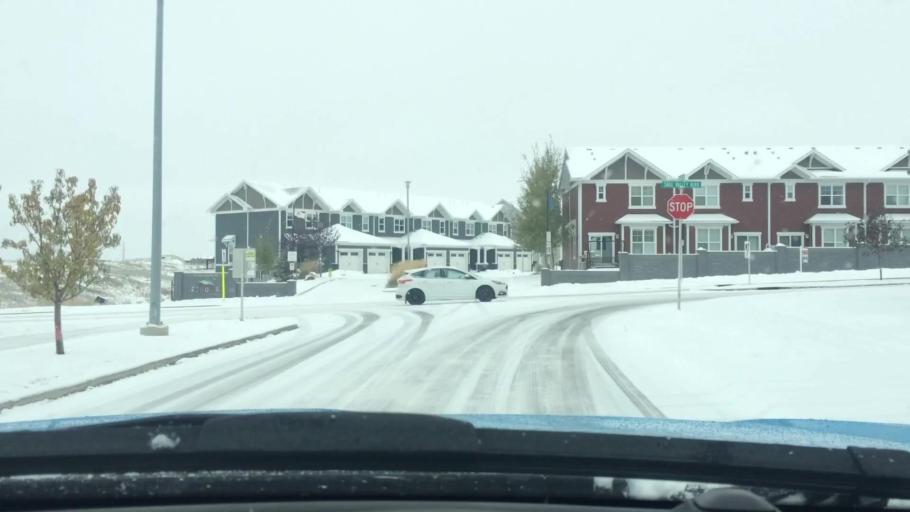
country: CA
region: Alberta
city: Calgary
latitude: 51.1762
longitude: -114.1538
